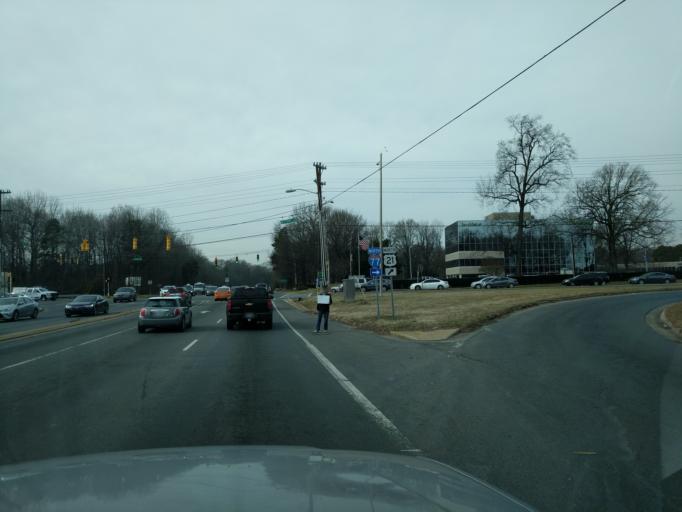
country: US
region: North Carolina
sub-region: Mecklenburg County
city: Charlotte
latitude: 35.1806
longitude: -80.8885
